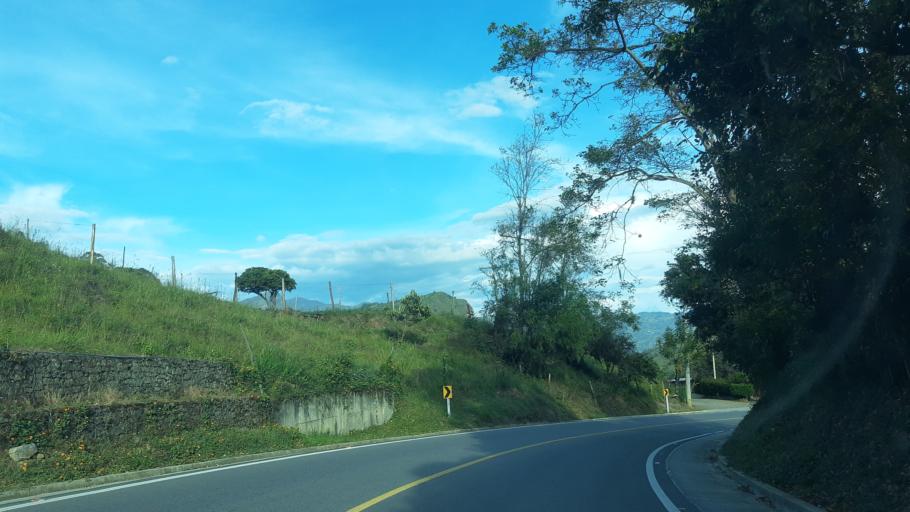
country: CO
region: Cundinamarca
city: Macheta
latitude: 5.0788
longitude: -73.5956
